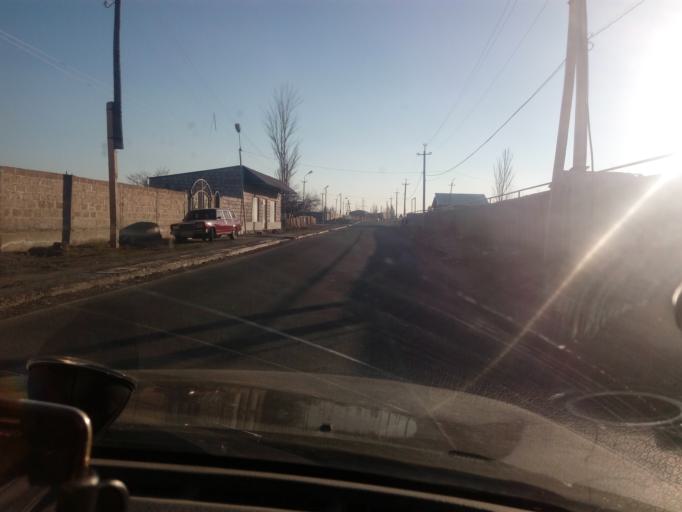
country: AM
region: Kotayk'i Marz
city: Nor Gyugh
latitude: 40.2660
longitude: 44.6534
